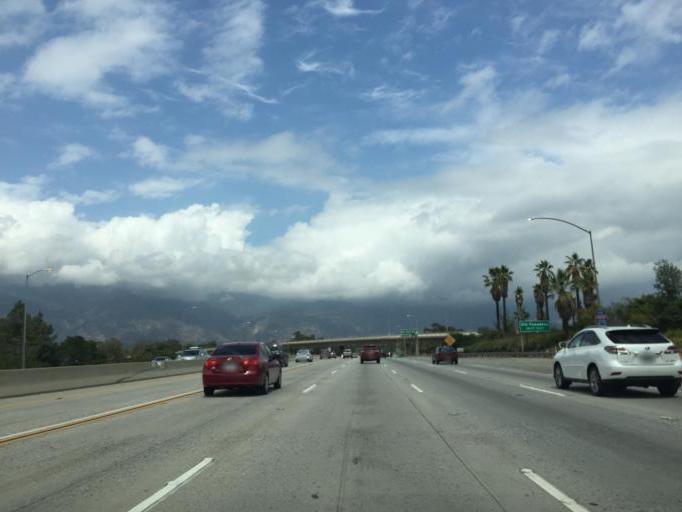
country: US
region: California
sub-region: Los Angeles County
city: Pasadena
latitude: 34.1482
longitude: -118.1579
